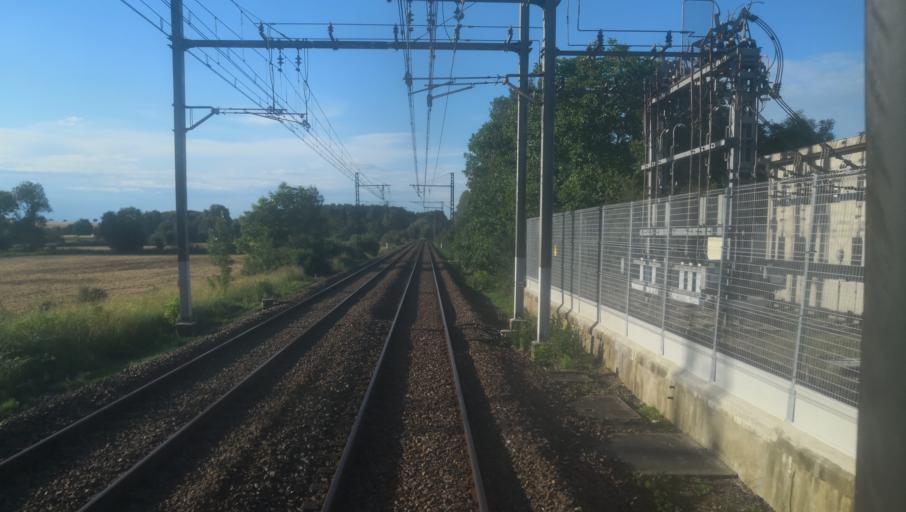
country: FR
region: Centre
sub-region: Departement de l'Indre
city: Sainte-Lizaigne
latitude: 47.0117
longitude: 2.0326
